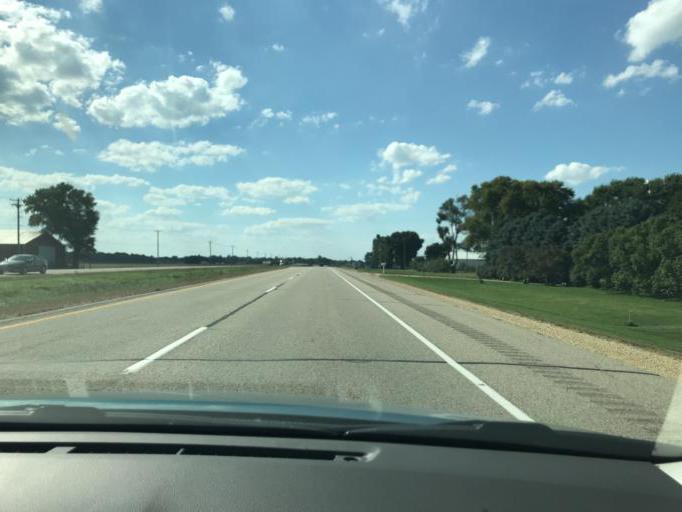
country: US
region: Wisconsin
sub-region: Kenosha County
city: Powers Lake
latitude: 42.5817
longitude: -88.3186
